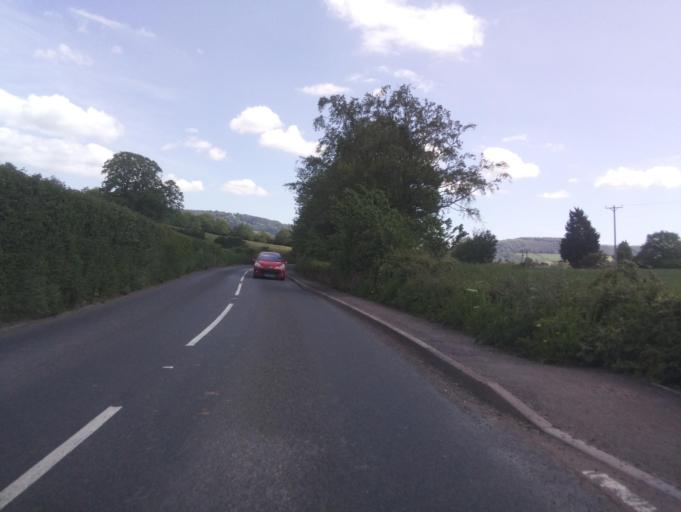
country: GB
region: Wales
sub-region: Monmouthshire
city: Monmouth
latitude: 51.8197
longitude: -2.7355
